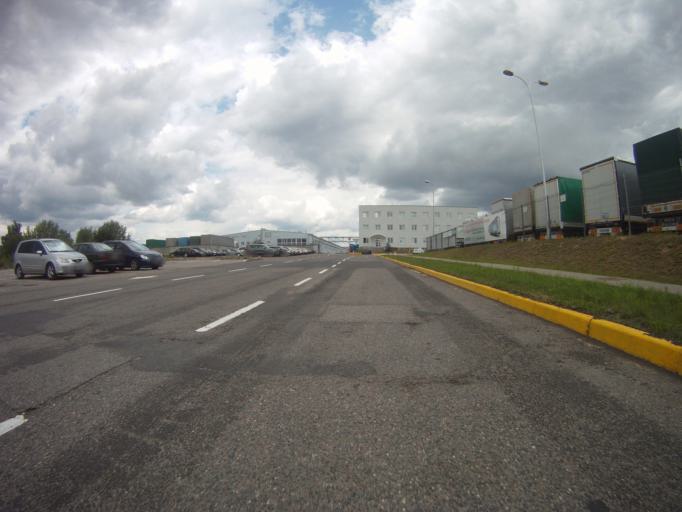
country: BY
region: Minsk
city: Malinovka
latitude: 53.8786
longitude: 27.4097
